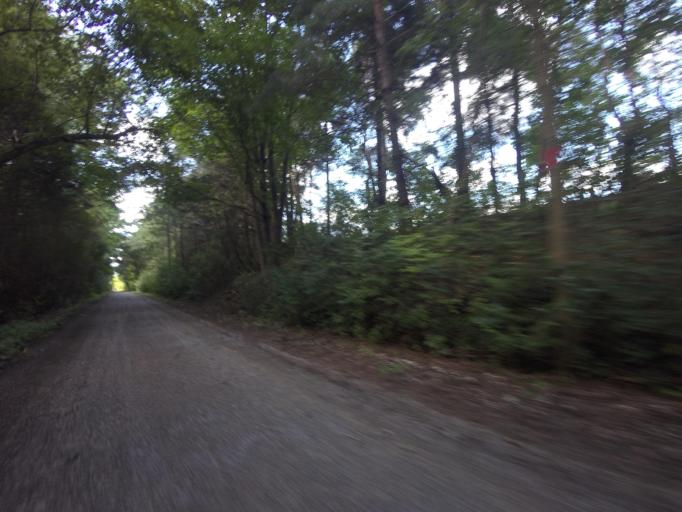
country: CA
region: Ontario
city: Huron East
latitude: 43.6733
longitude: -81.2826
